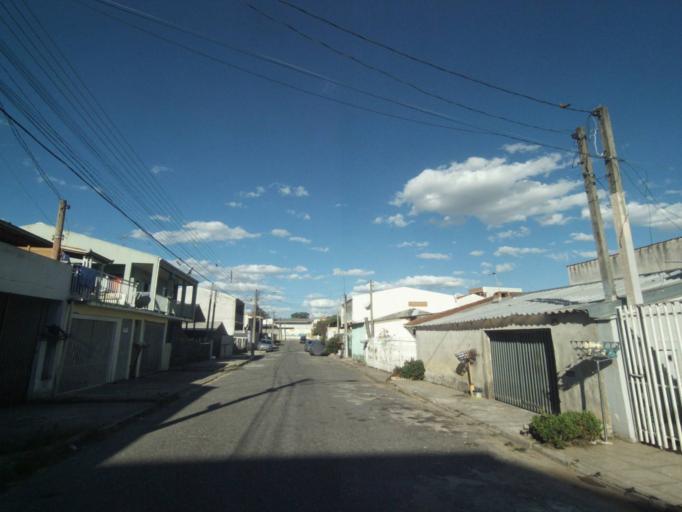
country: BR
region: Parana
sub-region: Curitiba
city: Curitiba
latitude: -25.5145
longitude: -49.3361
